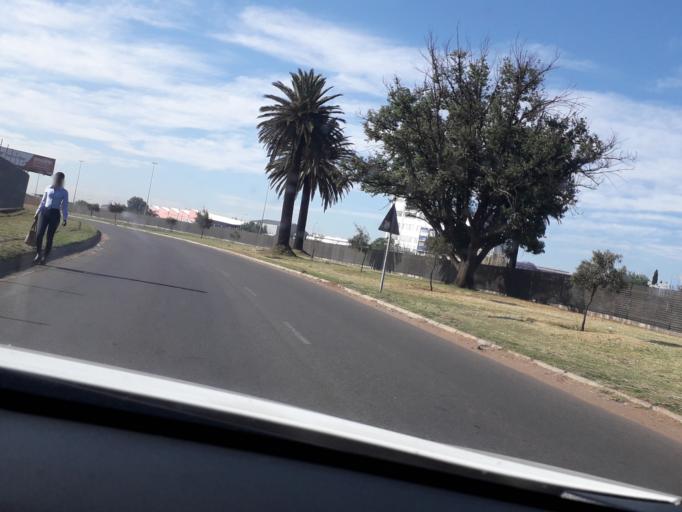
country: ZA
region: Gauteng
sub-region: Ekurhuleni Metropolitan Municipality
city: Germiston
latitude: -26.1649
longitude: 28.1889
